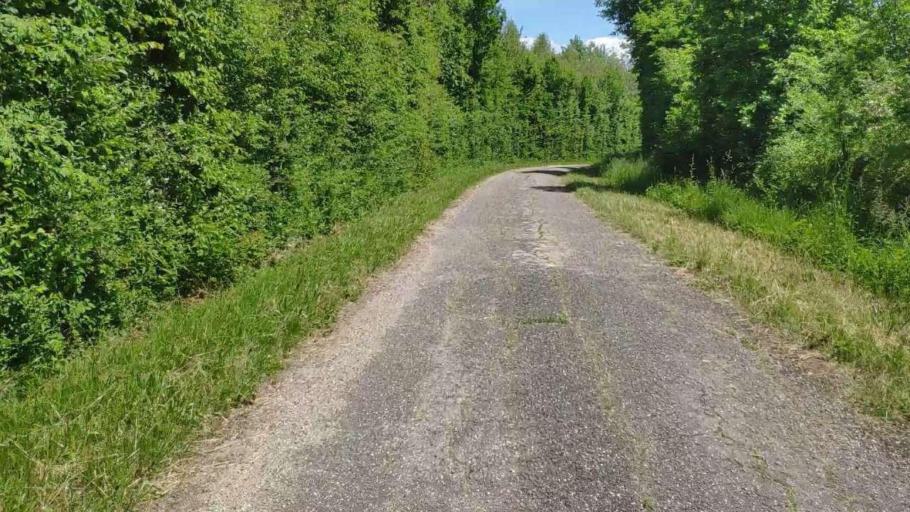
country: FR
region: Franche-Comte
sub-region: Departement du Jura
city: Bletterans
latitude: 46.7831
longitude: 5.4544
